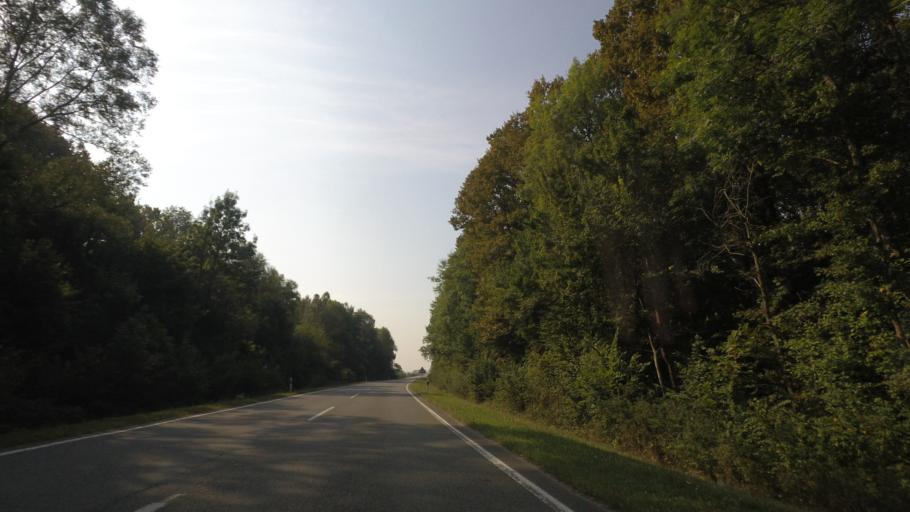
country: HR
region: Sisacko-Moslavacka
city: Novska
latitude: 45.3212
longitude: 16.9492
